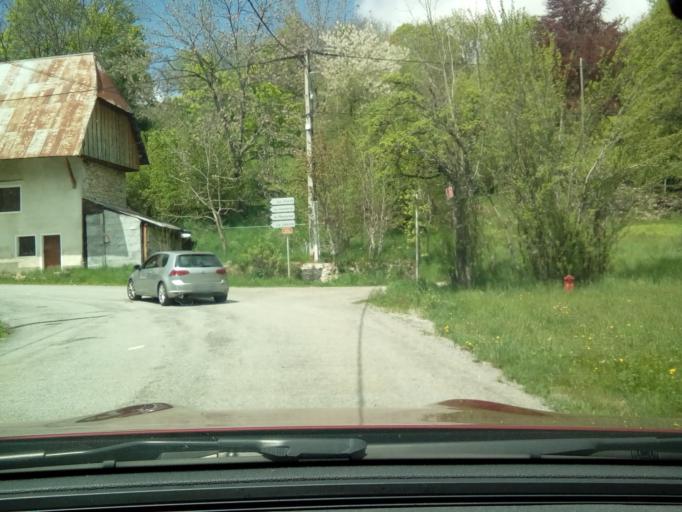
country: FR
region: Rhone-Alpes
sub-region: Departement de la Savoie
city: Barby
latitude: 45.6208
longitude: 6.0009
